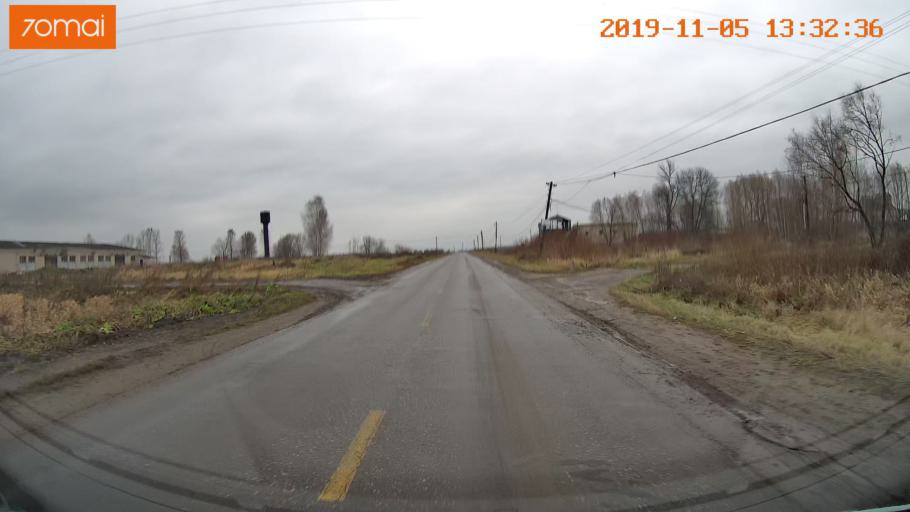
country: RU
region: Ivanovo
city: Shuya
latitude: 56.8845
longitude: 41.3974
